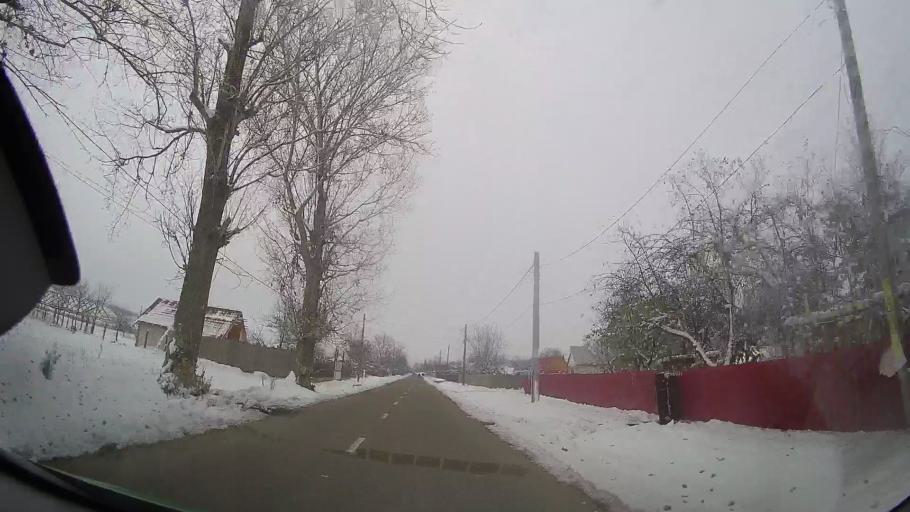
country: RO
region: Neamt
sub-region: Comuna Bozieni
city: Bozieni
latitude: 46.8308
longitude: 27.1785
